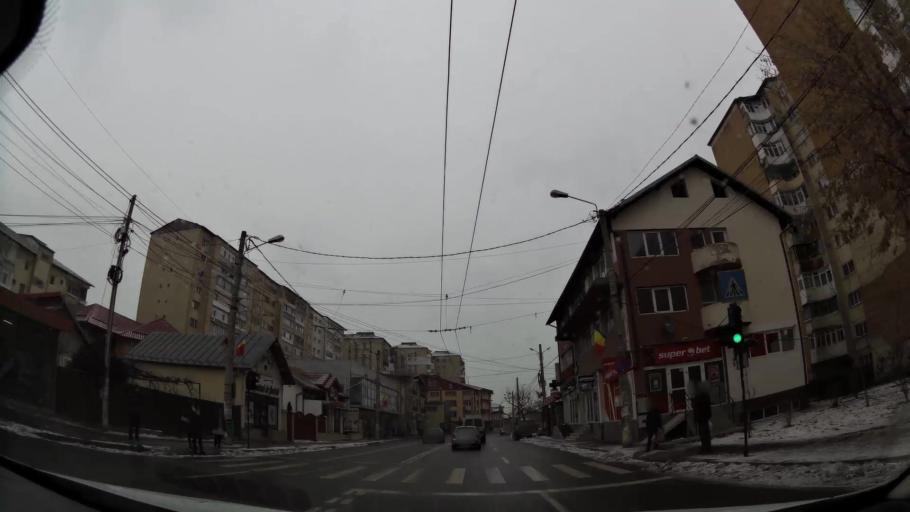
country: RO
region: Dambovita
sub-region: Municipiul Targoviste
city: Targoviste
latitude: 44.9308
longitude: 25.4490
